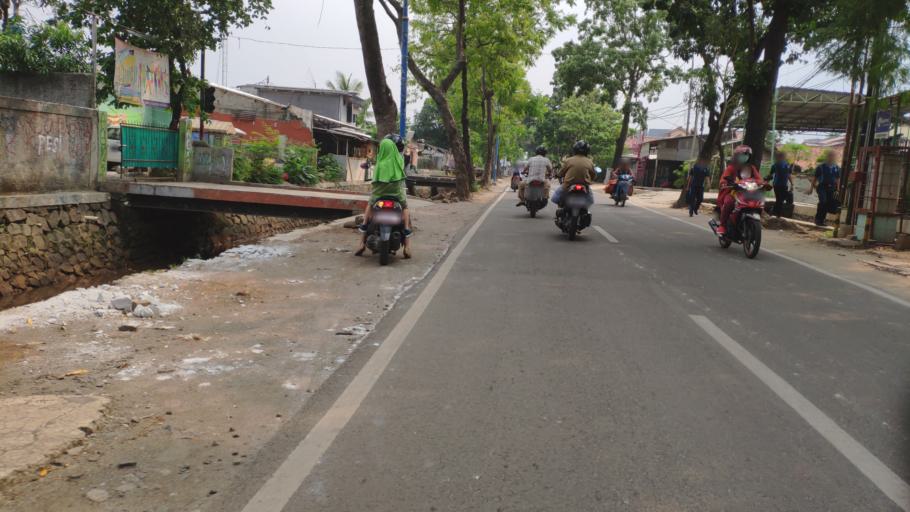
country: ID
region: West Java
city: Depok
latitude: -6.3478
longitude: 106.8137
